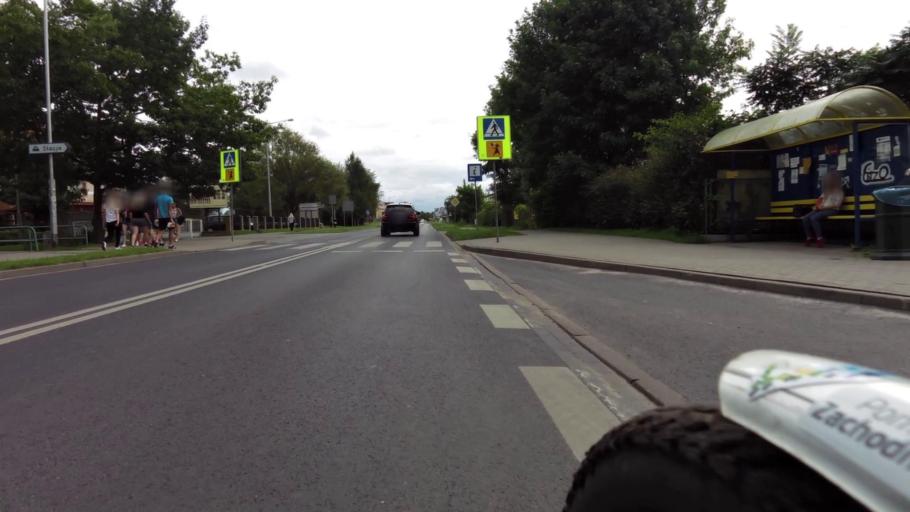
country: PL
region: West Pomeranian Voivodeship
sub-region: Powiat koszalinski
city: Mielno
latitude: 54.2547
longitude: 16.0541
